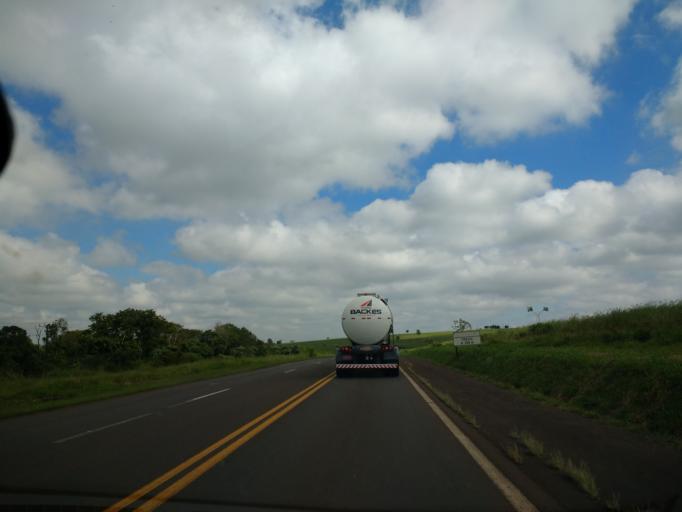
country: BR
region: Parana
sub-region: Cruzeiro Do Oeste
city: Cruzeiro do Oeste
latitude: -23.7725
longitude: -53.0169
